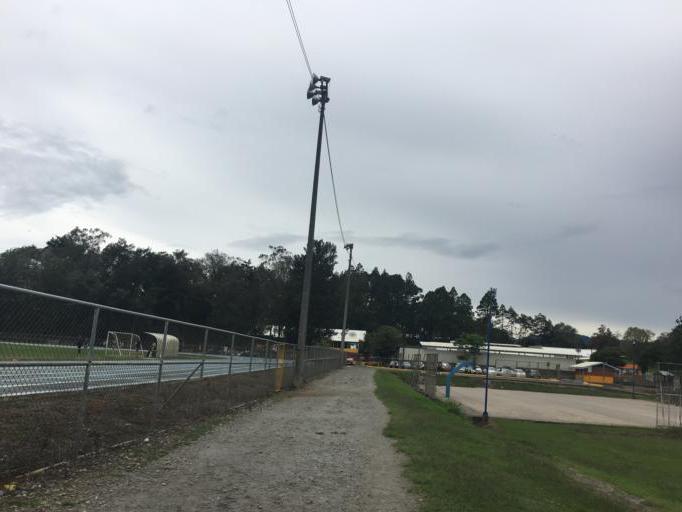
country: CR
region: Cartago
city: Cartago
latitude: 9.8566
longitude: -83.9092
